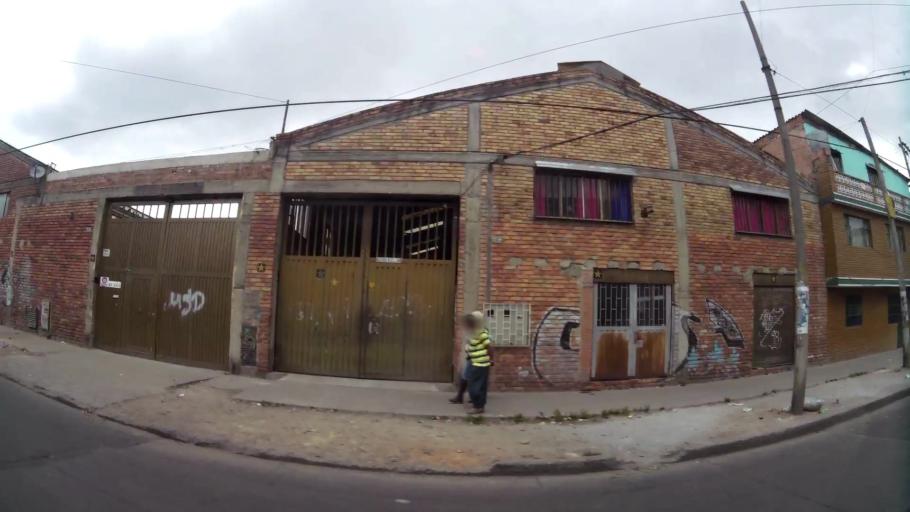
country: CO
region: Bogota D.C.
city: Bogota
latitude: 4.6052
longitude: -74.1349
